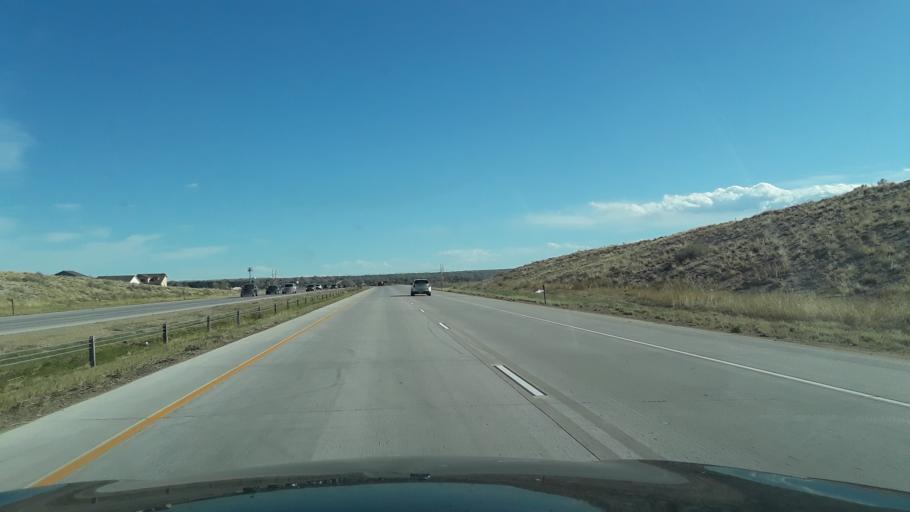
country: US
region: Colorado
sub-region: Pueblo County
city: Pueblo
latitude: 38.2875
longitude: -104.6635
